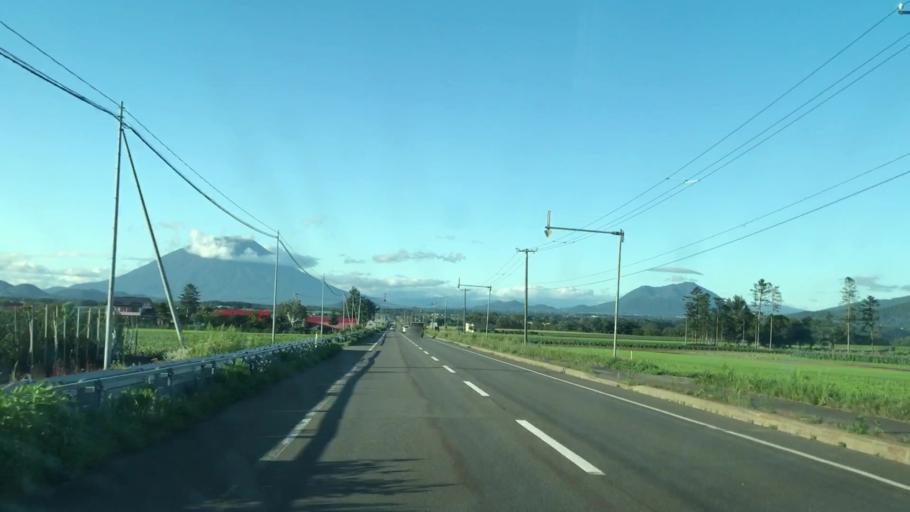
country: JP
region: Hokkaido
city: Date
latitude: 42.6347
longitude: 140.8013
